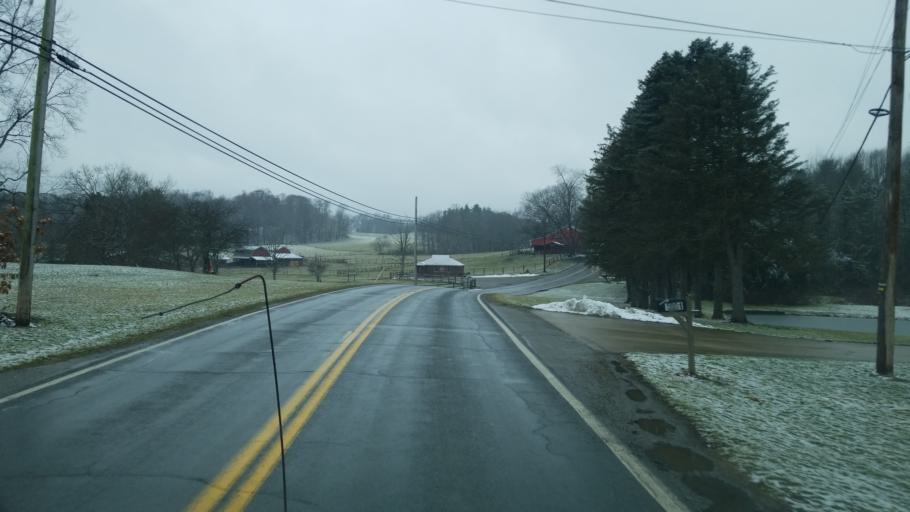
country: US
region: Ohio
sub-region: Portage County
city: Mantua
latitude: 41.2842
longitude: -81.2473
